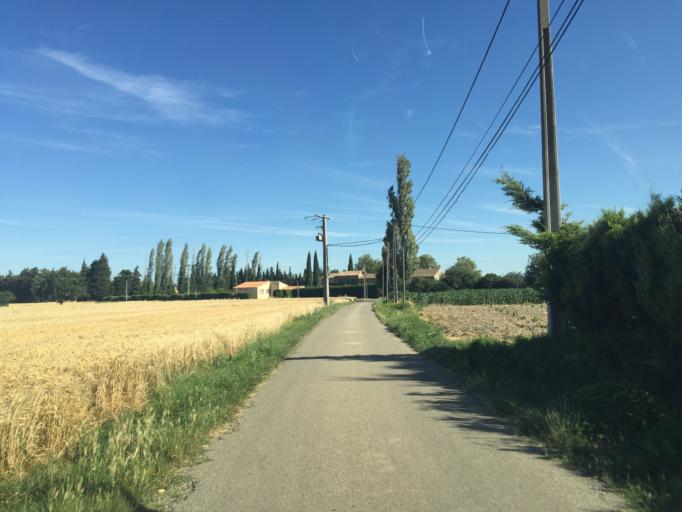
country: FR
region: Provence-Alpes-Cote d'Azur
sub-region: Departement du Vaucluse
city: Caderousse
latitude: 44.1196
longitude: 4.7298
